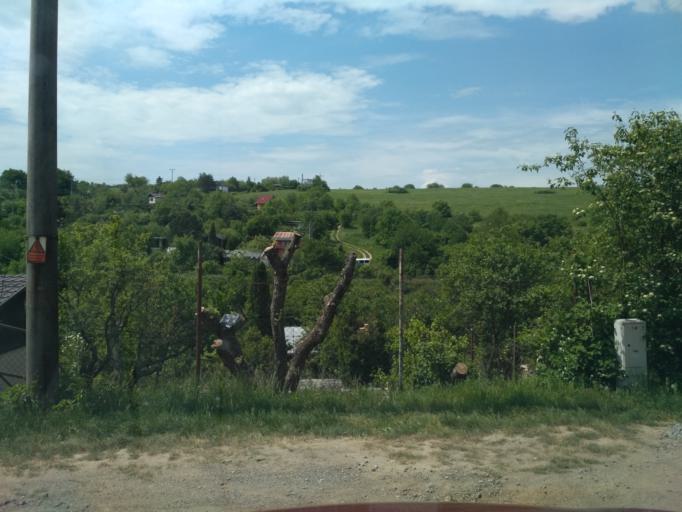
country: SK
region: Kosicky
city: Kosice
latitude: 48.7284
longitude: 21.2241
